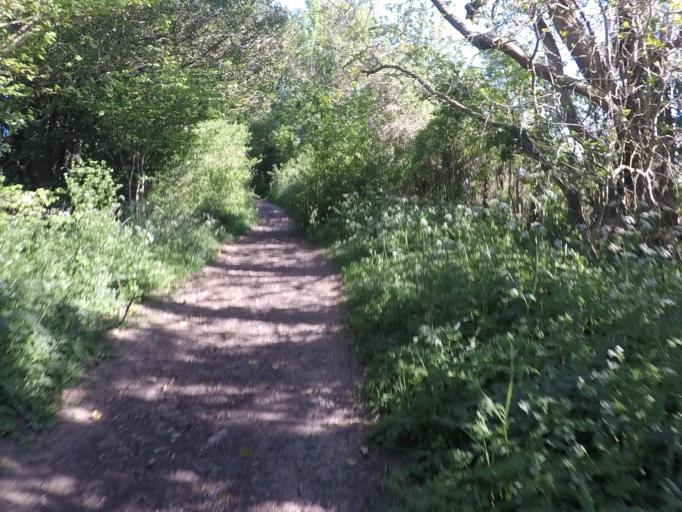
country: GB
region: England
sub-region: Oxfordshire
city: Charlbury
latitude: 51.8618
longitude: -1.4670
